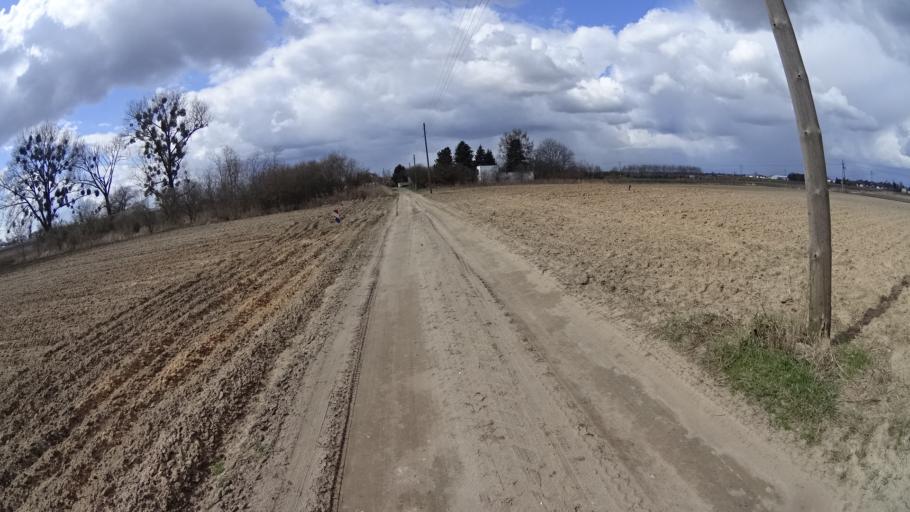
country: PL
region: Masovian Voivodeship
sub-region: Powiat warszawski zachodni
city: Jozefow
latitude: 52.2174
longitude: 20.7320
